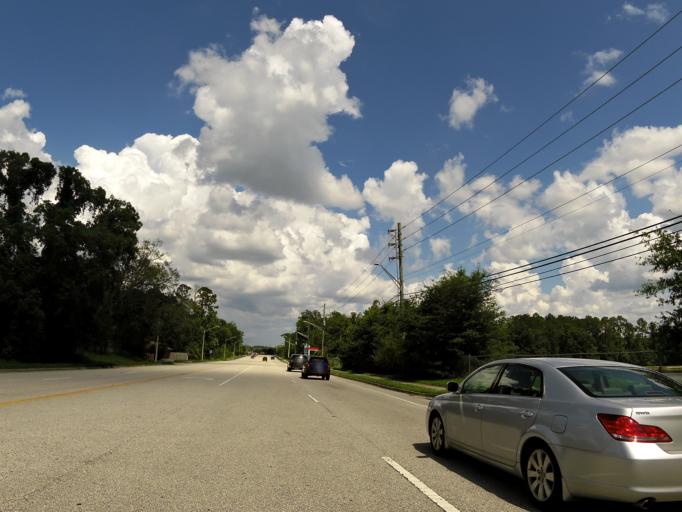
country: US
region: Florida
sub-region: Saint Johns County
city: Fruit Cove
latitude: 30.1446
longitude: -81.5595
